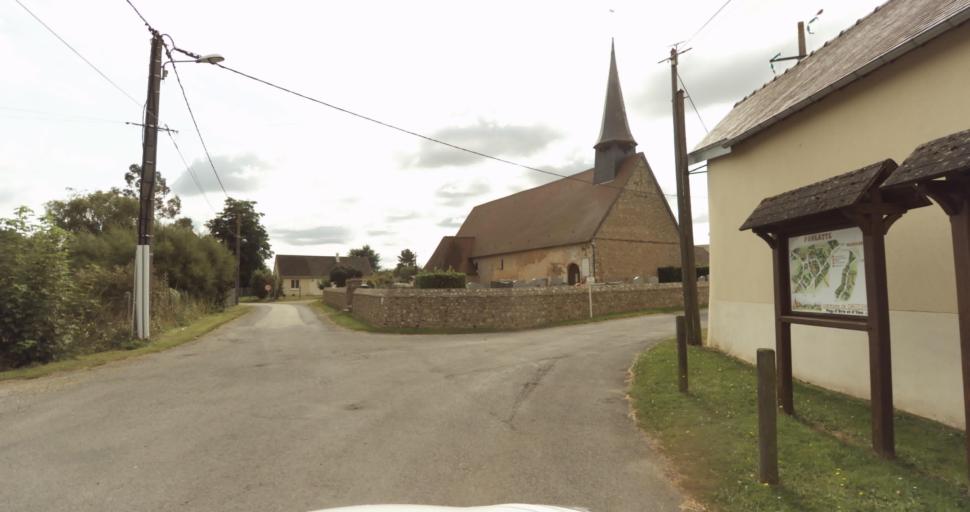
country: FR
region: Haute-Normandie
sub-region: Departement de l'Eure
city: Tillieres-sur-Avre
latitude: 48.7962
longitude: 1.0983
